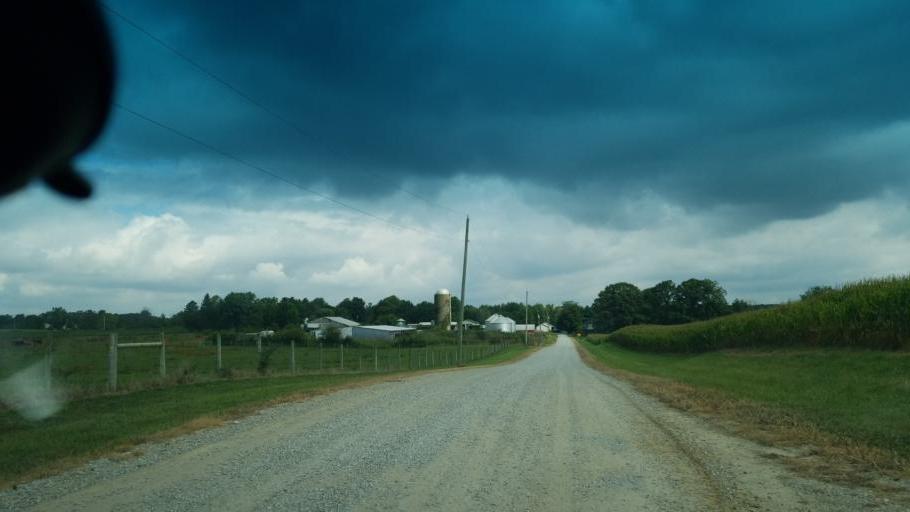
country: US
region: Ohio
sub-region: Knox County
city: Centerburg
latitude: 40.2702
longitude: -82.6720
